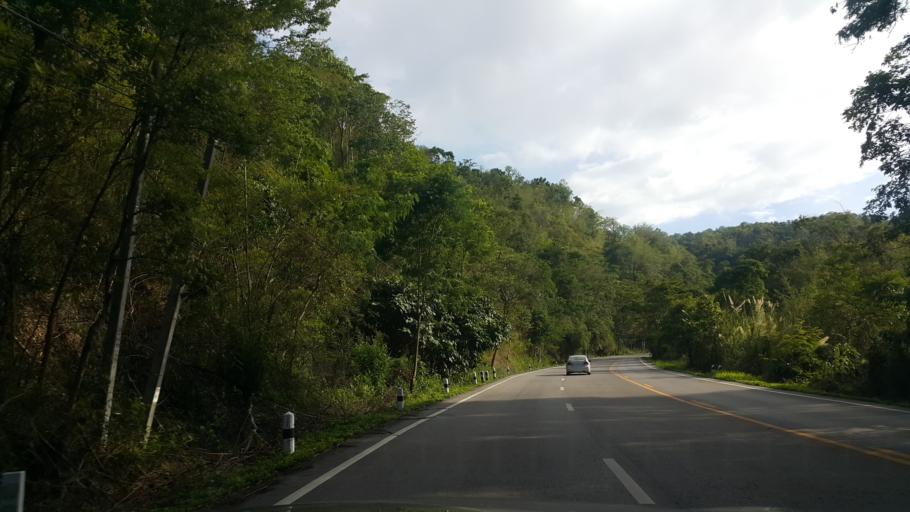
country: TH
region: Phayao
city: Phayao
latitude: 19.0635
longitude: 99.8025
